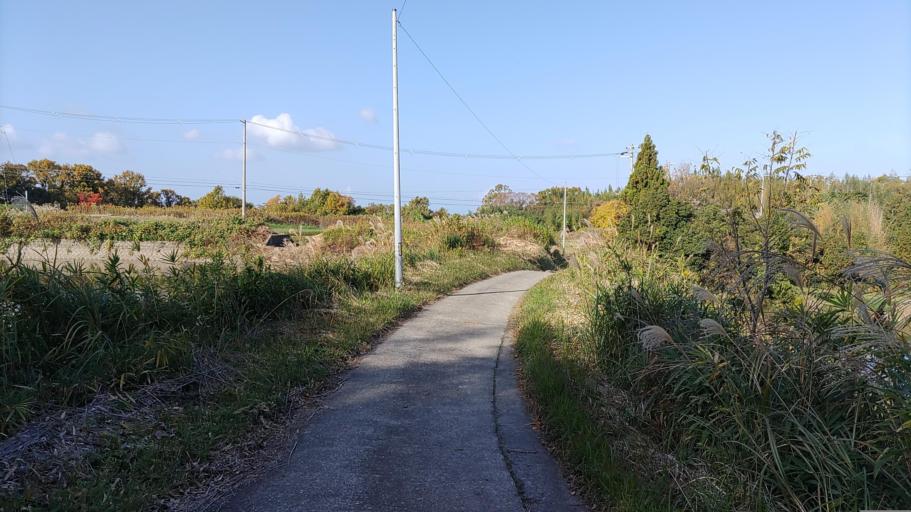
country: JP
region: Hyogo
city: Sumoto
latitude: 34.3852
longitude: 134.8139
